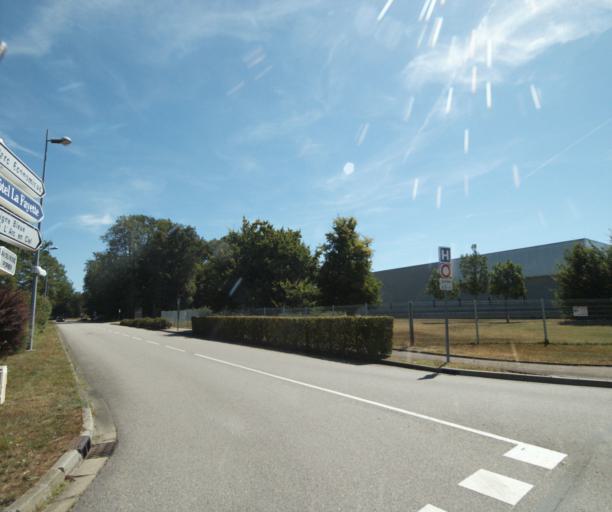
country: FR
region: Lorraine
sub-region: Departement des Vosges
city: Dogneville
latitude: 48.2020
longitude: 6.4617
